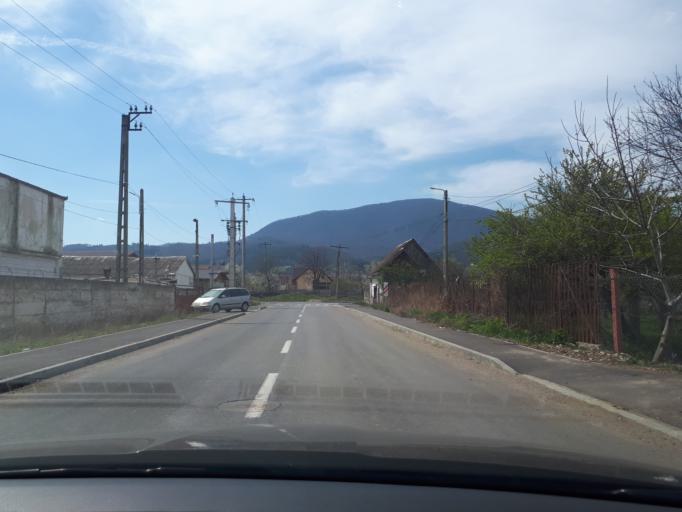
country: RO
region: Brasov
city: Codlea
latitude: 45.7042
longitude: 25.4588
